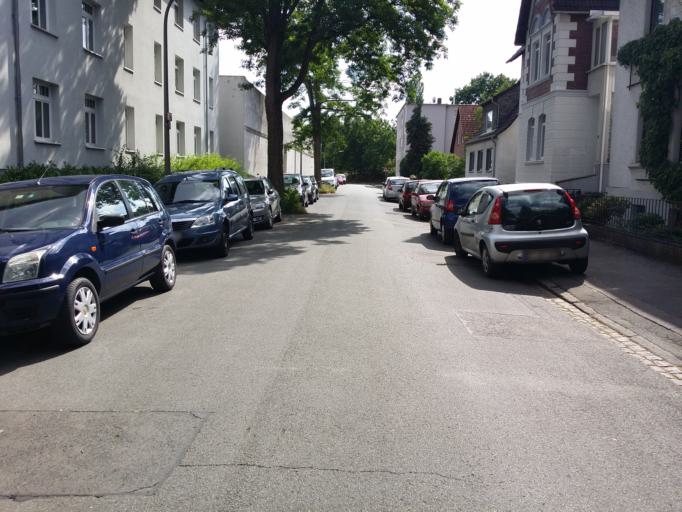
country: DE
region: Lower Saxony
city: Braunschweig
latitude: 52.2813
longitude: 10.5515
